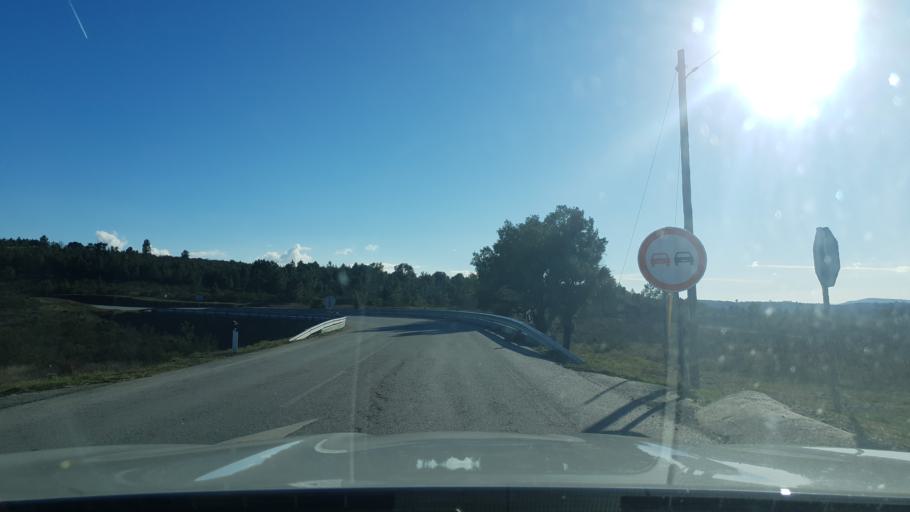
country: PT
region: Braganca
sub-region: Freixo de Espada A Cinta
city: Freixo de Espada a Cinta
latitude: 41.1206
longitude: -6.8210
